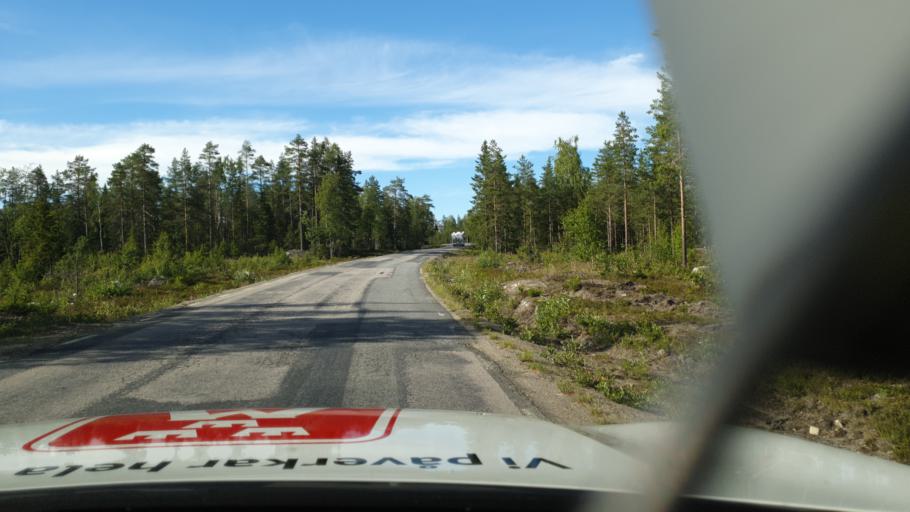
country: SE
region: Vaesterbotten
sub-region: Umea Kommun
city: Saevar
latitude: 63.8606
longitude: 20.5940
